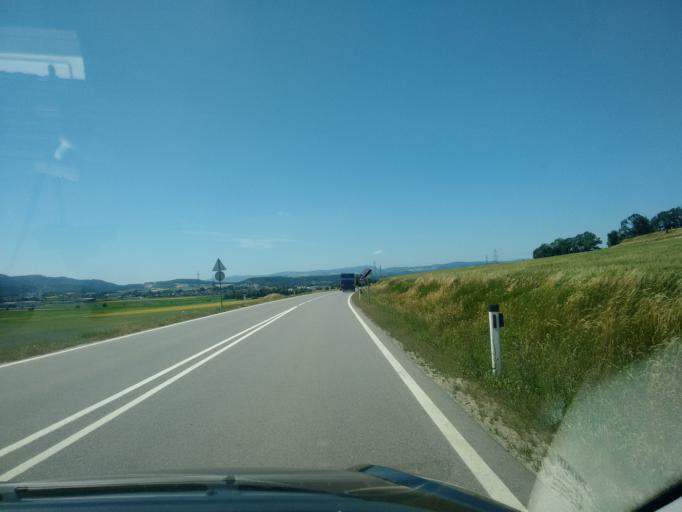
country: AT
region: Lower Austria
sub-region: Politischer Bezirk Sankt Polten
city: Haunoldstein
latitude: 48.1936
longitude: 15.4301
